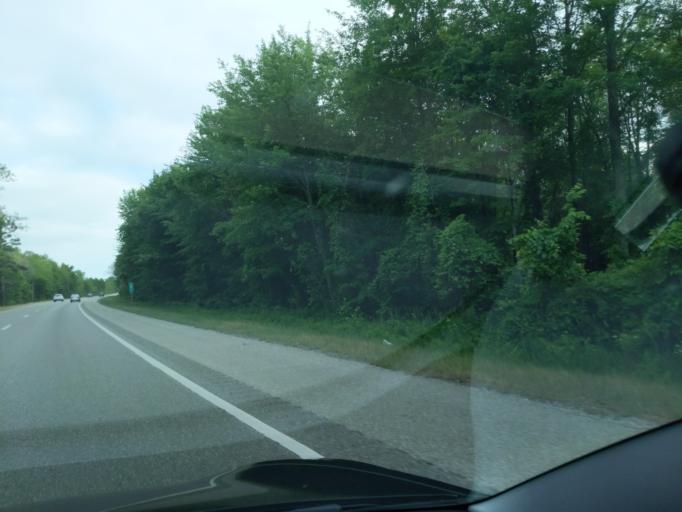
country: US
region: Michigan
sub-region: Muskegon County
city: Lakewood Club
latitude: 43.3463
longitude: -86.2468
